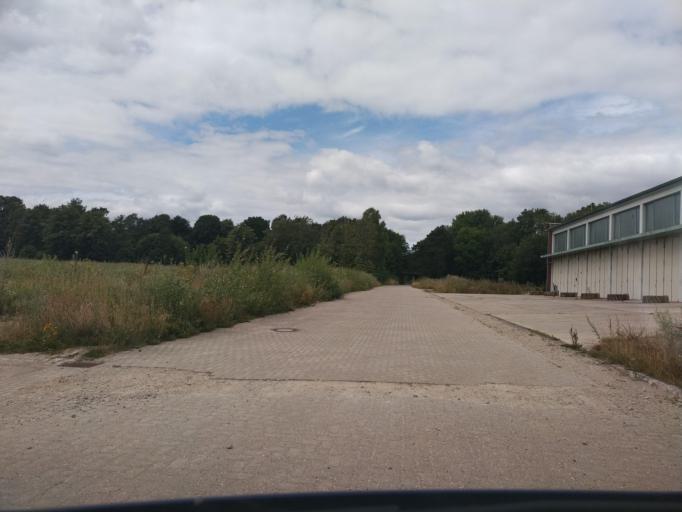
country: DE
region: Schleswig-Holstein
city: Fahrdorf
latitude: 54.5191
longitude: 9.5956
